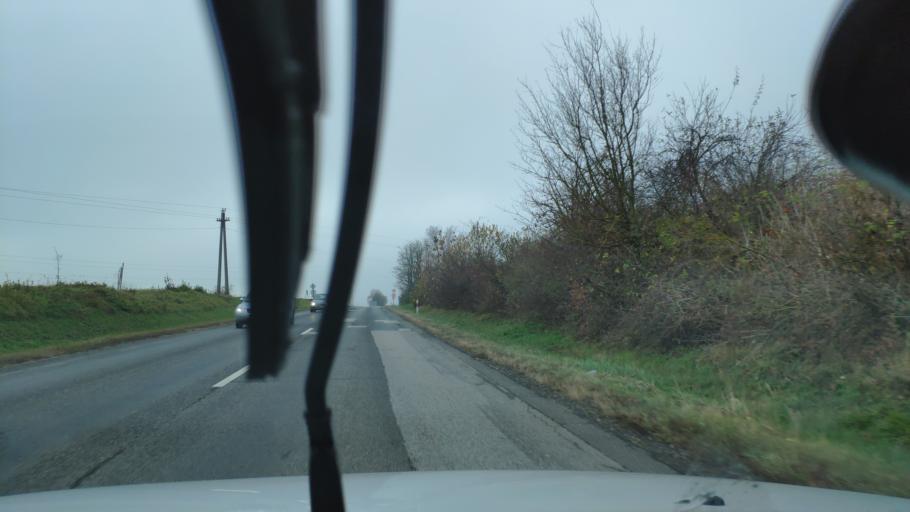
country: HU
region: Zala
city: Nagykanizsa
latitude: 46.4715
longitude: 17.0430
